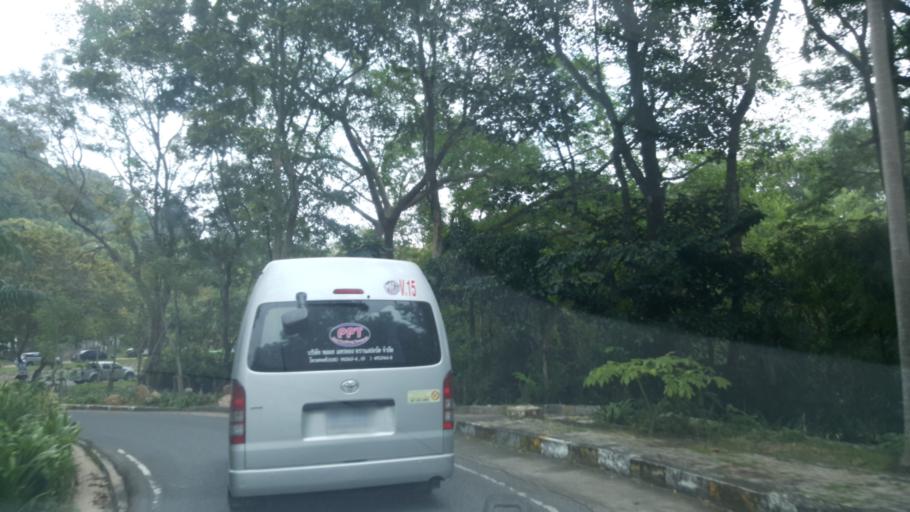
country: TH
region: Chon Buri
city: Ban Bueng
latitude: 13.2178
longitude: 101.0569
